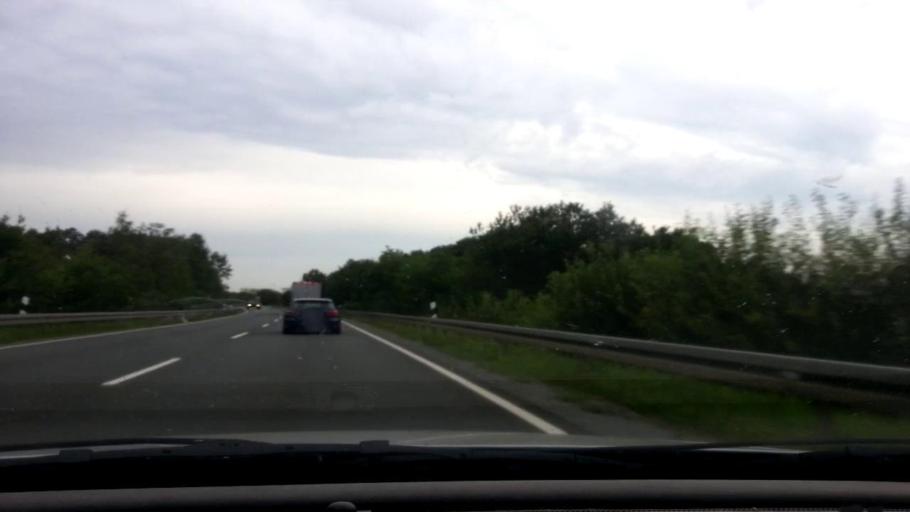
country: DE
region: Bavaria
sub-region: Upper Franconia
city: Seybothenreuth
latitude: 49.8972
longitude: 11.7093
